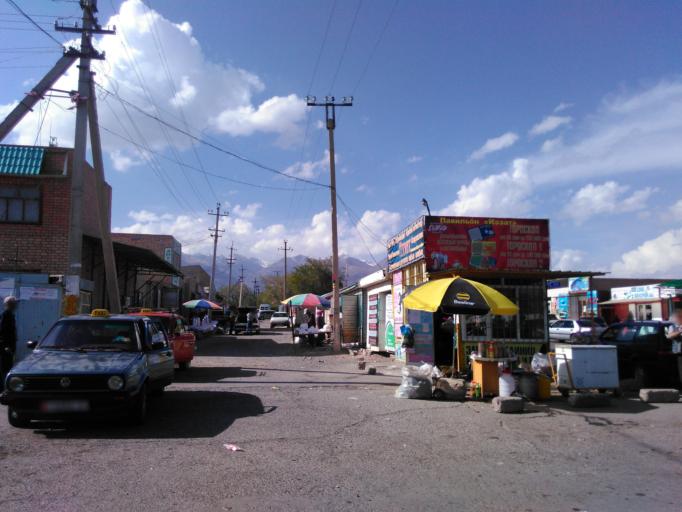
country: KG
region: Ysyk-Koel
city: Balykchy
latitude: 42.4549
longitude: 76.1785
